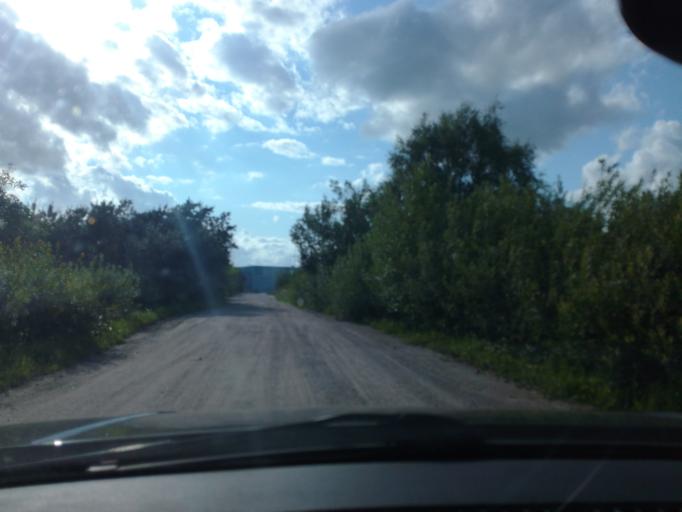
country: LT
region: Alytaus apskritis
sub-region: Alytus
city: Alytus
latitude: 54.4172
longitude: 24.0152
